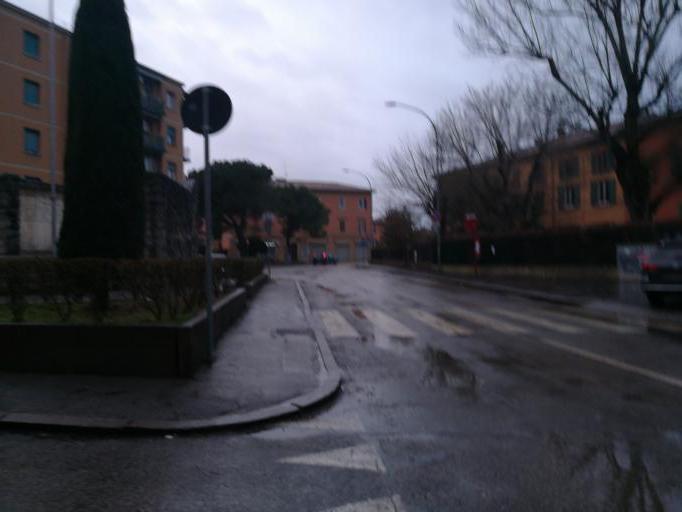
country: IT
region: Emilia-Romagna
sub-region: Provincia di Bologna
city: Progresso
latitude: 44.5483
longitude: 11.3559
